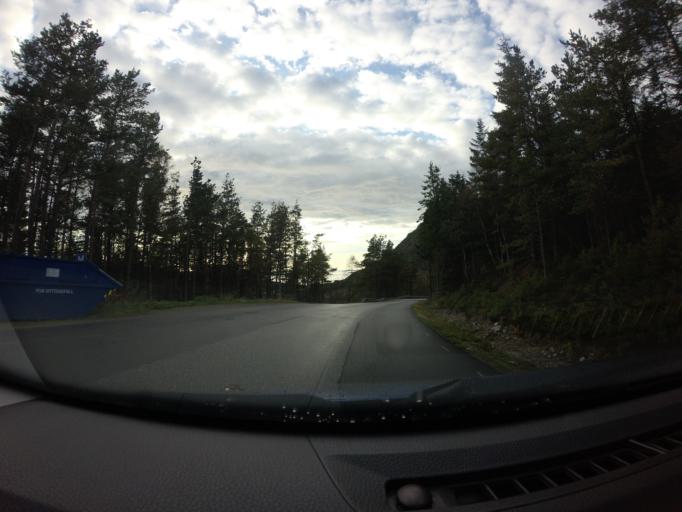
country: NO
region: Rogaland
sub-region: Strand
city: Jorpeland
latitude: 58.9994
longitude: 6.1118
